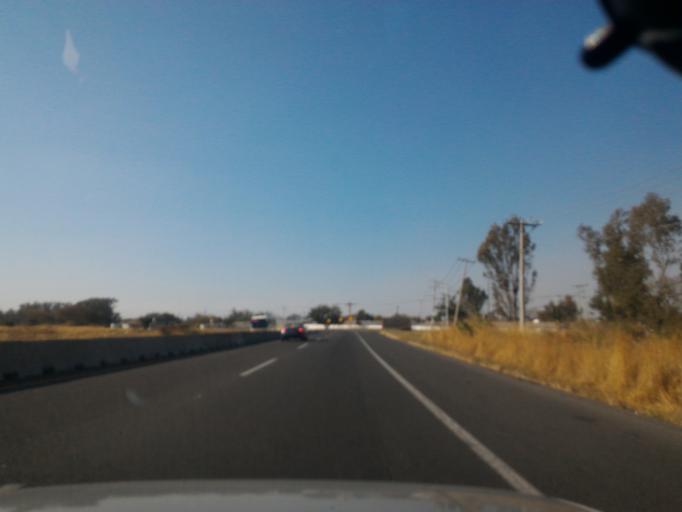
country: MX
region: Jalisco
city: Atequiza
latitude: 20.3970
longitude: -103.1479
